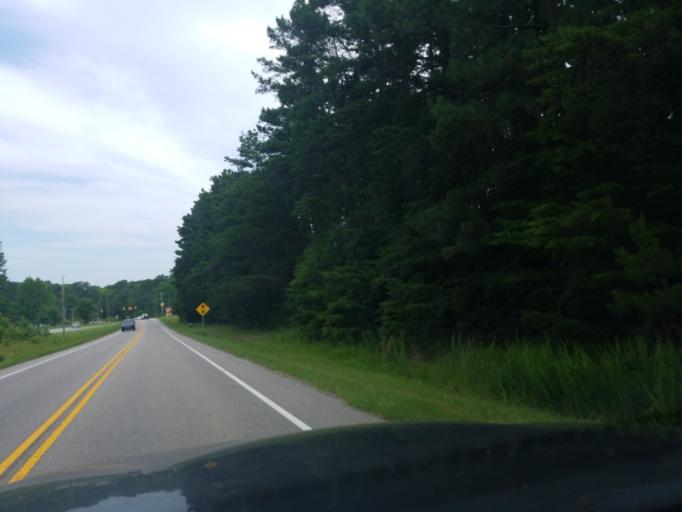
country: US
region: North Carolina
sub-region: Durham County
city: Durham
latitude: 36.1232
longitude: -78.9400
